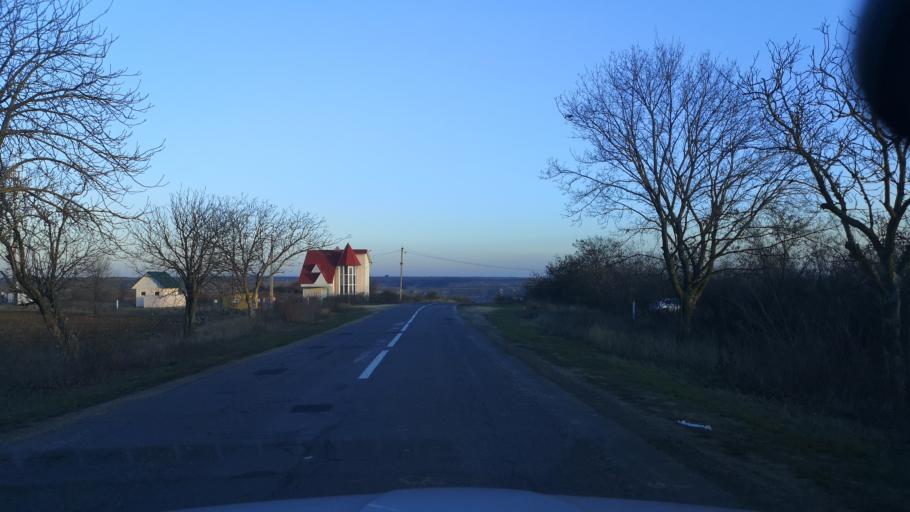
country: MD
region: Telenesti
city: Cocieri
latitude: 47.3114
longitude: 28.9635
